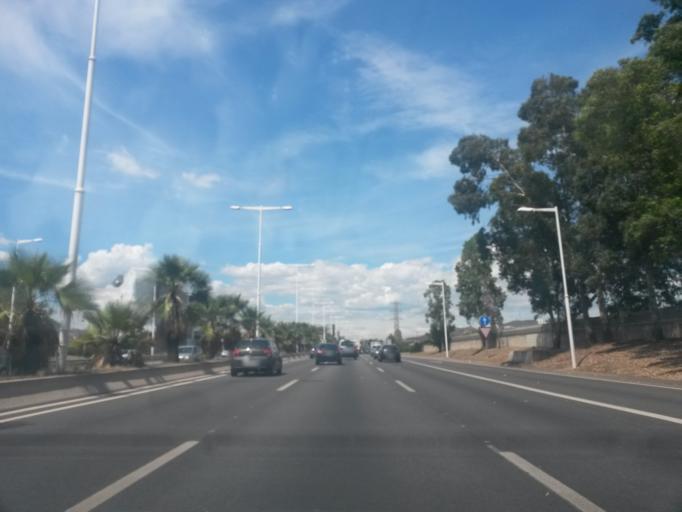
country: ES
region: Catalonia
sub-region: Provincia de Barcelona
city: Sant Adria de Besos
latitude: 41.4311
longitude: 2.2121
